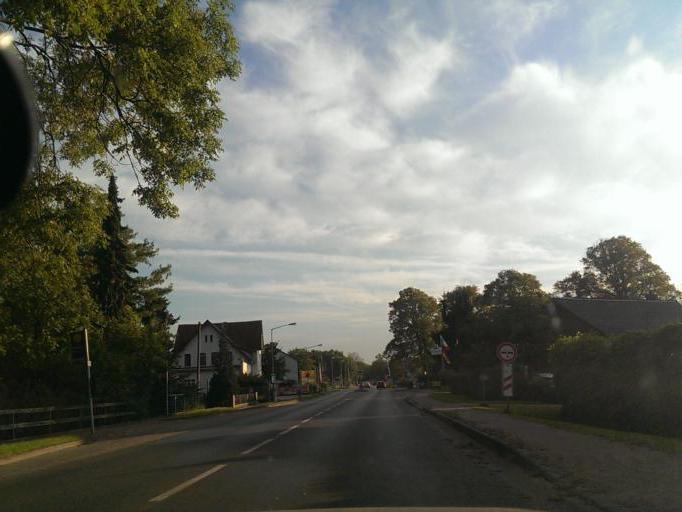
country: DE
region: Lower Saxony
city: Elze
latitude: 52.5810
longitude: 9.7286
